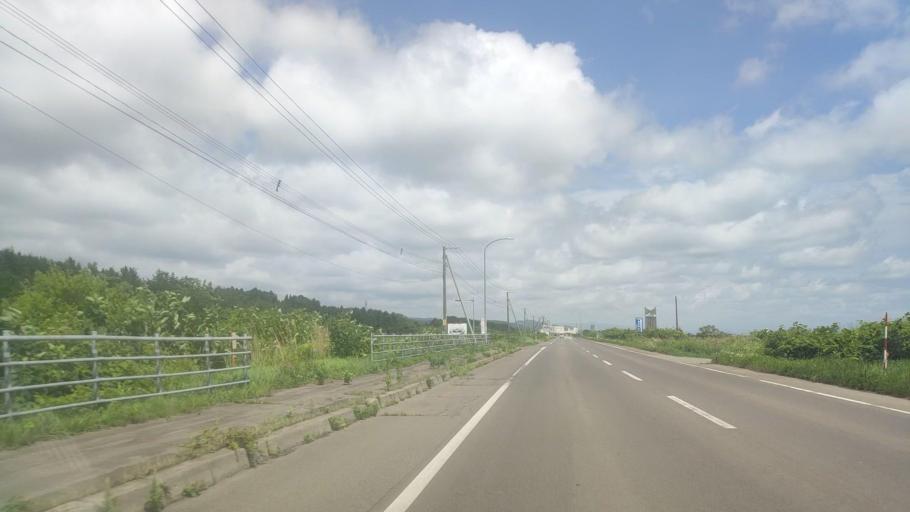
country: JP
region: Hokkaido
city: Niseko Town
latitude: 42.3740
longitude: 140.2910
